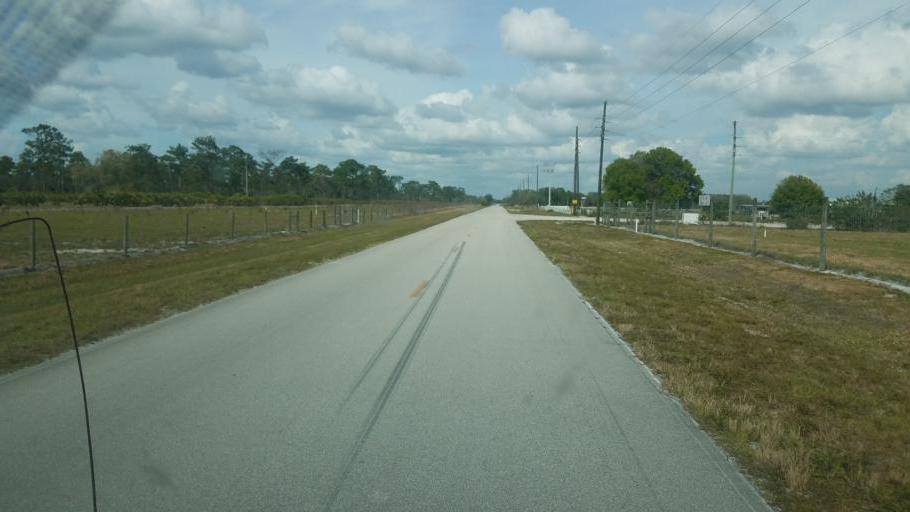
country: US
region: Florida
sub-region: Okeechobee County
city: Cypress Quarters
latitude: 27.5002
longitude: -80.7749
